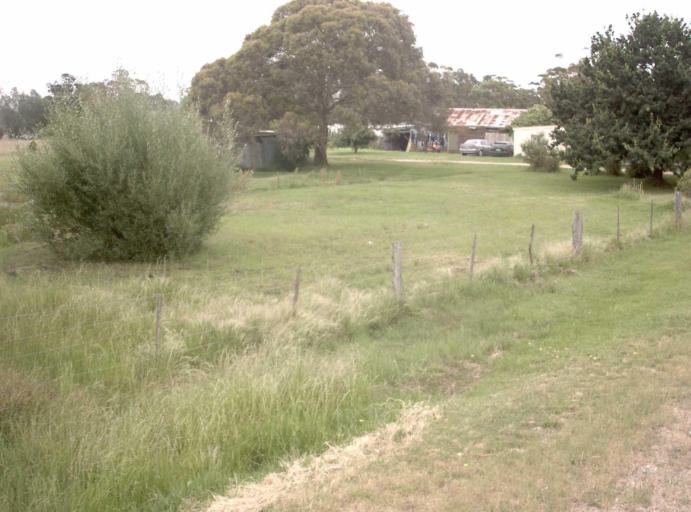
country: AU
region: Victoria
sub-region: East Gippsland
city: Bairnsdale
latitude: -37.8287
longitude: 147.4338
